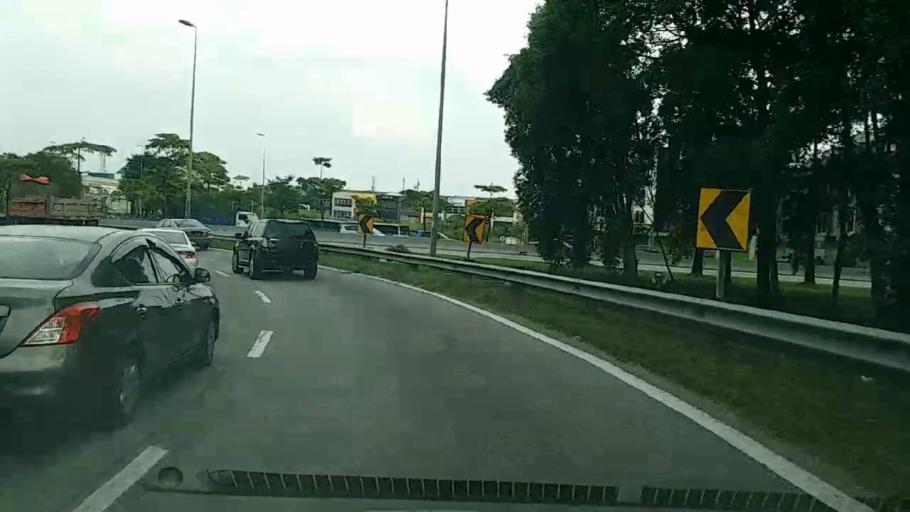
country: MY
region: Selangor
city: Subang Jaya
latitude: 3.0208
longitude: 101.6088
